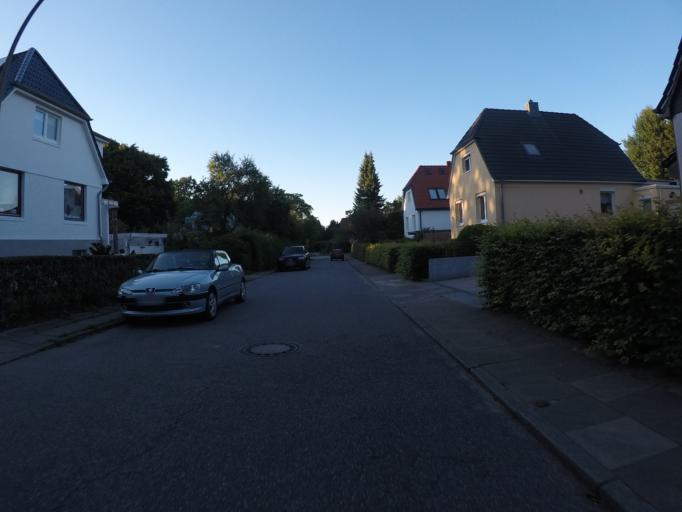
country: DE
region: Hamburg
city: Langenhorn
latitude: 53.6607
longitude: 10.0185
